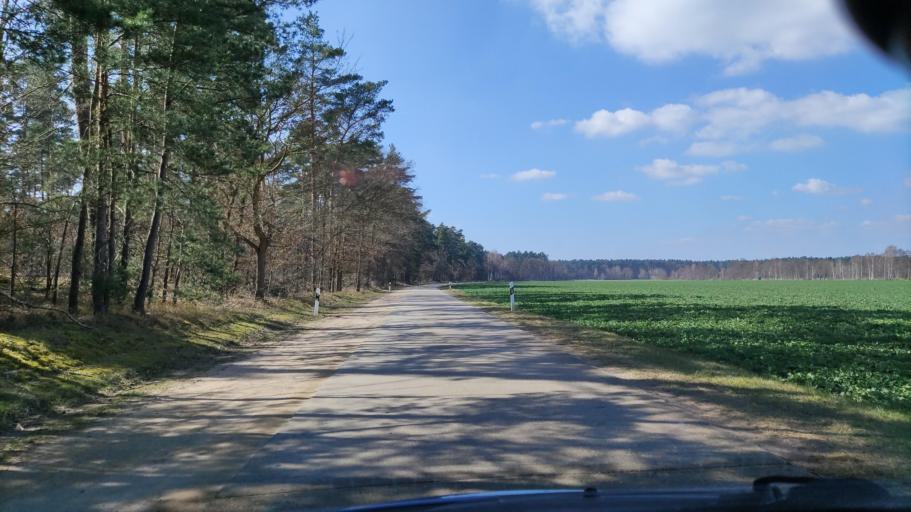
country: DE
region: Lower Saxony
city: Trebel
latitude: 52.9939
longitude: 11.3077
